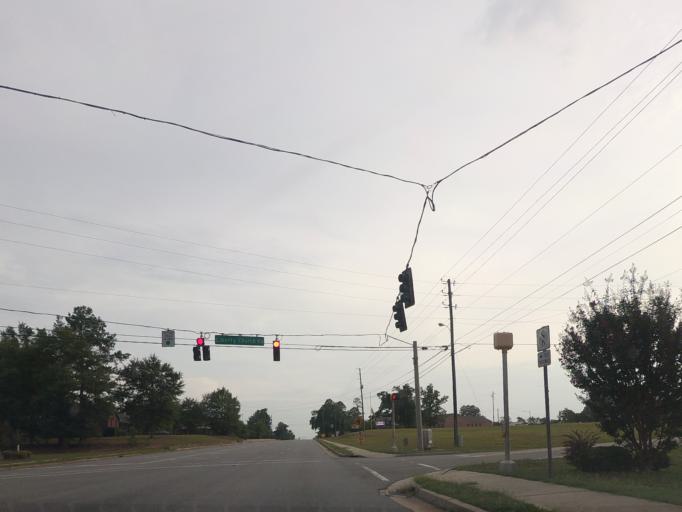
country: US
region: Georgia
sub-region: Houston County
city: Centerville
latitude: 32.7251
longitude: -83.6846
